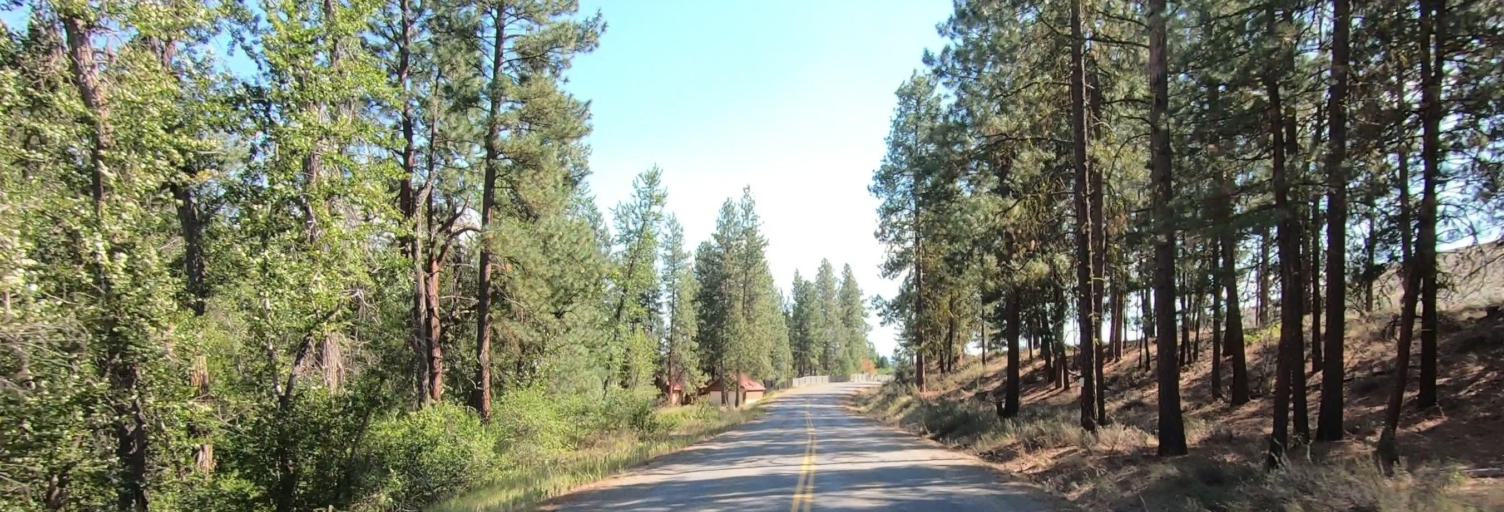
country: US
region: Washington
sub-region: Okanogan County
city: Brewster
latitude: 48.5064
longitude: -120.1873
